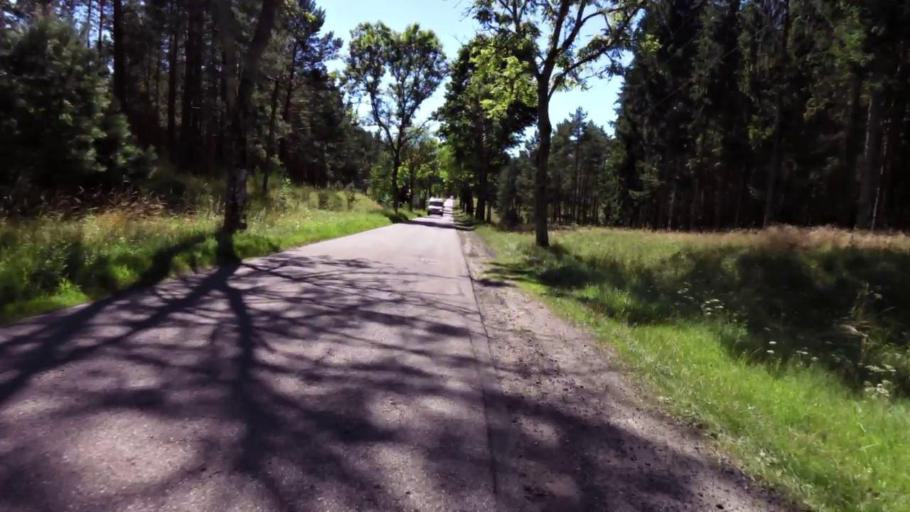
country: PL
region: West Pomeranian Voivodeship
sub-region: Powiat szczecinecki
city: Bialy Bor
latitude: 53.8861
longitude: 16.8131
